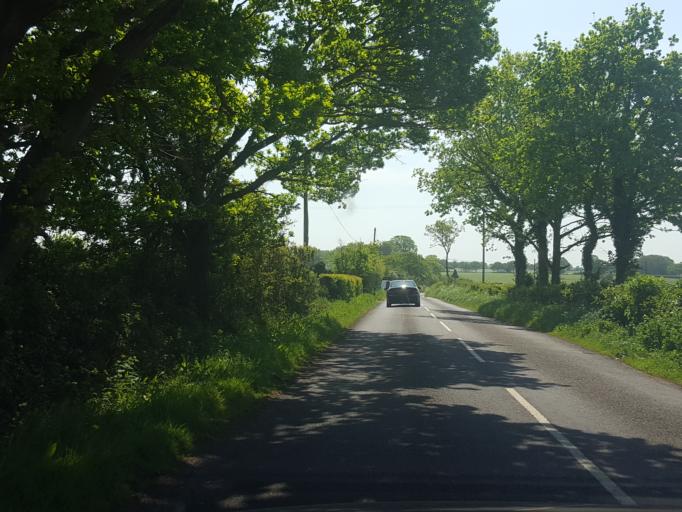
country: GB
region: England
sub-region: Essex
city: Great Bentley
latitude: 51.8562
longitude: 1.0858
